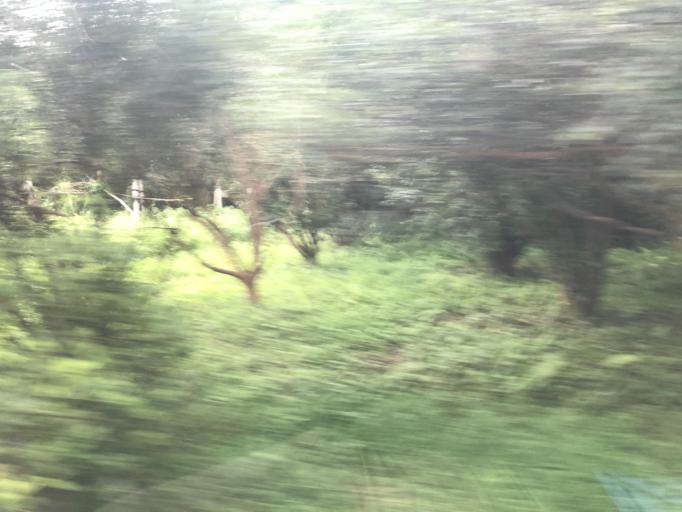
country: TW
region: Taiwan
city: Daxi
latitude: 24.9207
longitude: 121.3586
